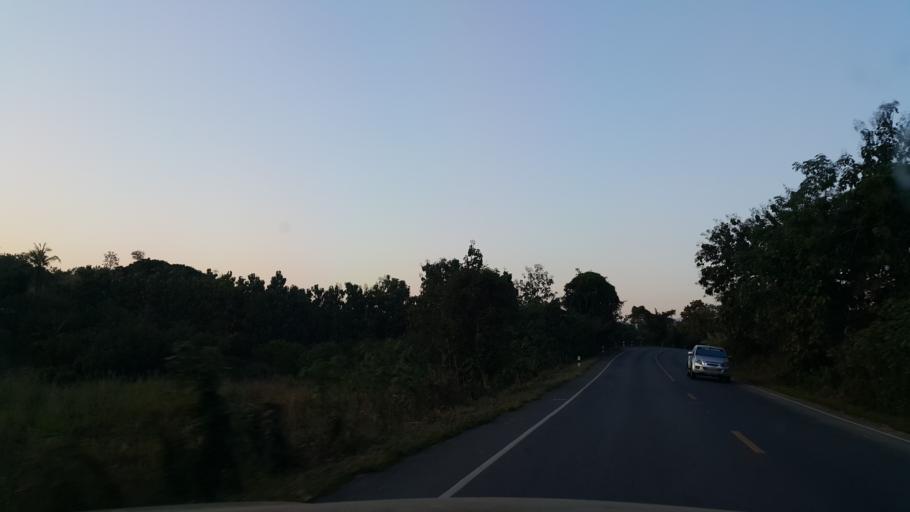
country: TH
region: Phrae
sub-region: Amphoe Wang Chin
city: Wang Chin
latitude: 17.8371
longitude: 99.6414
